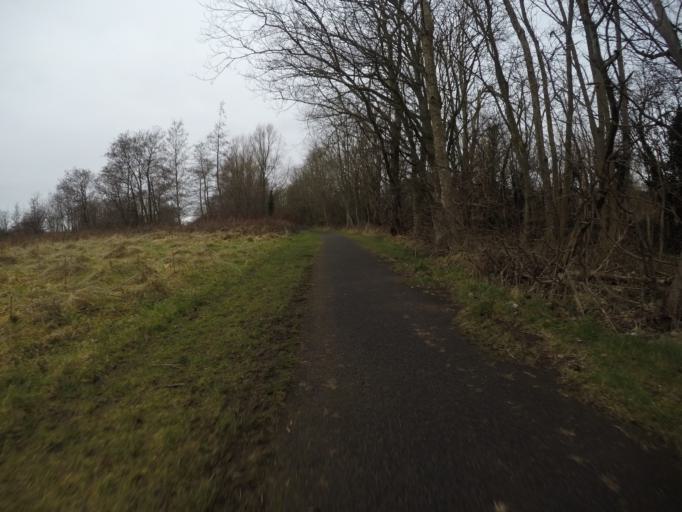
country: GB
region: Scotland
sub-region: North Ayrshire
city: Kilwinning
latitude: 55.6444
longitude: -4.6882
